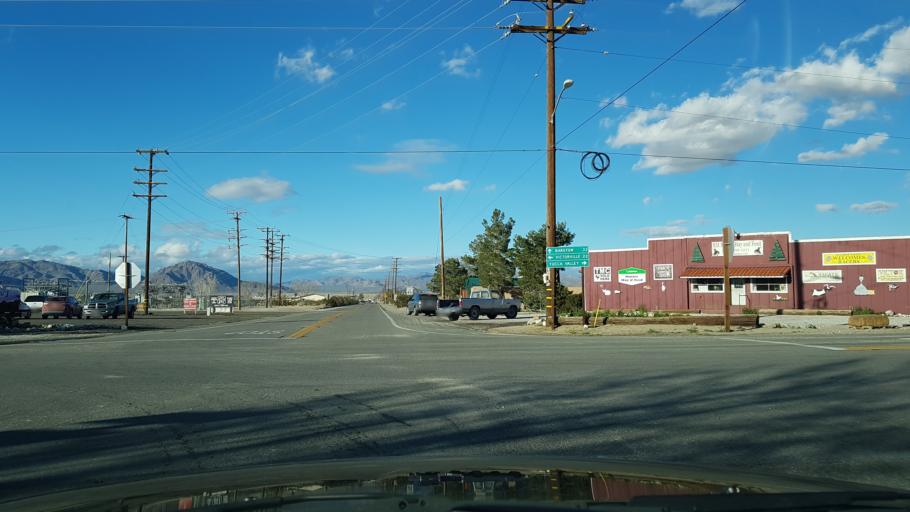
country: US
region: California
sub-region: San Bernardino County
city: Lucerne Valley
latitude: 34.4437
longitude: -116.9459
